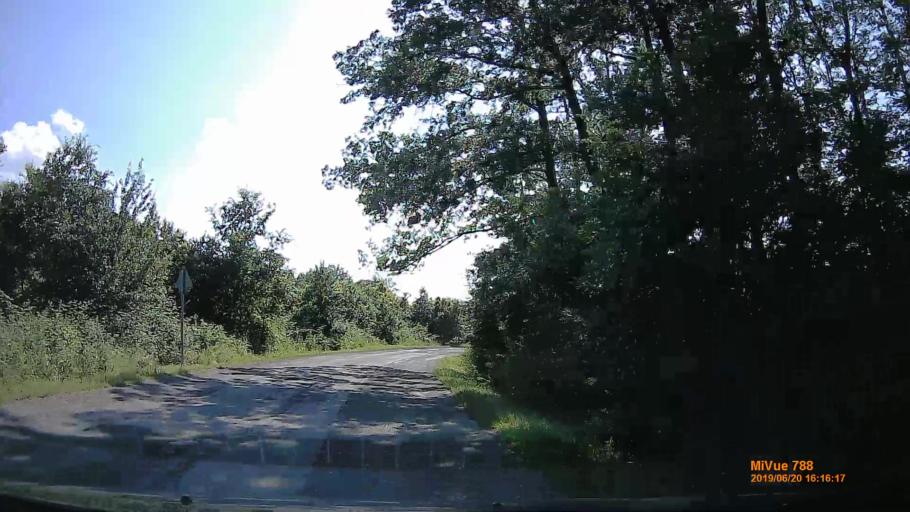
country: HU
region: Baranya
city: Buekkoesd
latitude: 46.0972
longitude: 18.0692
